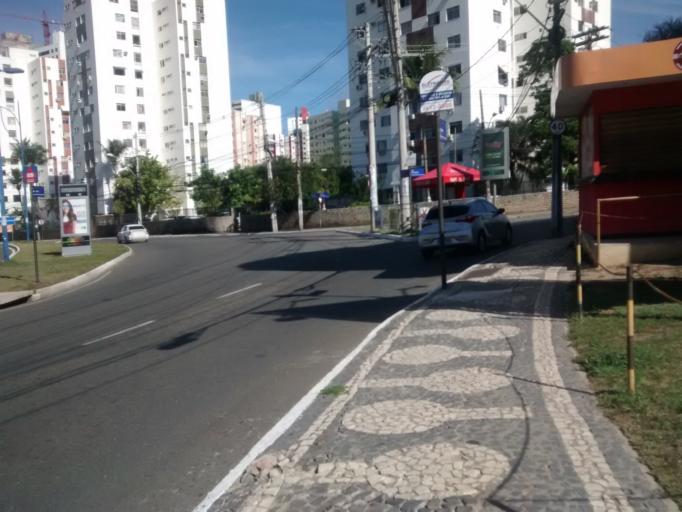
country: BR
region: Bahia
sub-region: Salvador
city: Salvador
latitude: -12.9693
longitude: -38.4390
